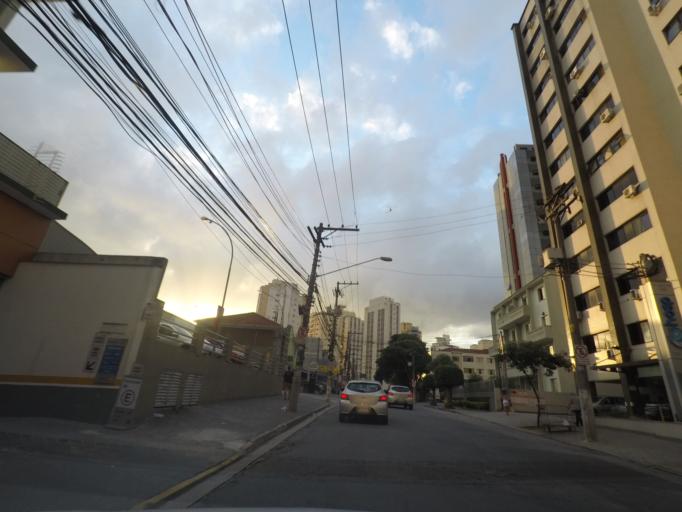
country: BR
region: Sao Paulo
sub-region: Sao Paulo
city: Sao Paulo
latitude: -23.4876
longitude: -46.6223
